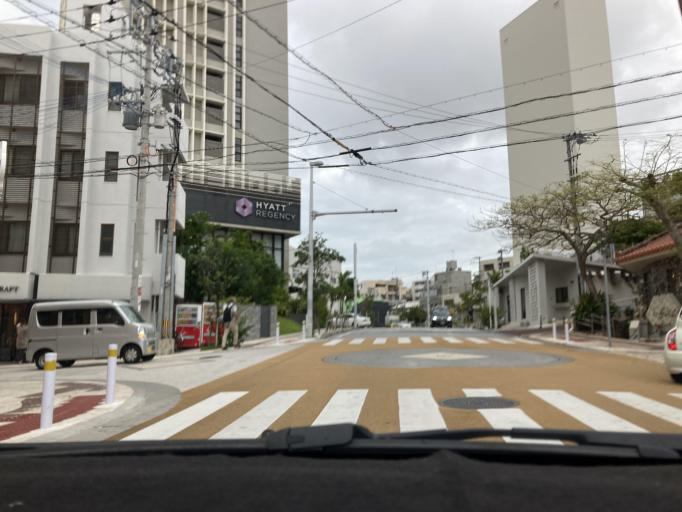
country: JP
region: Okinawa
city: Naha-shi
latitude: 26.2137
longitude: 127.6903
